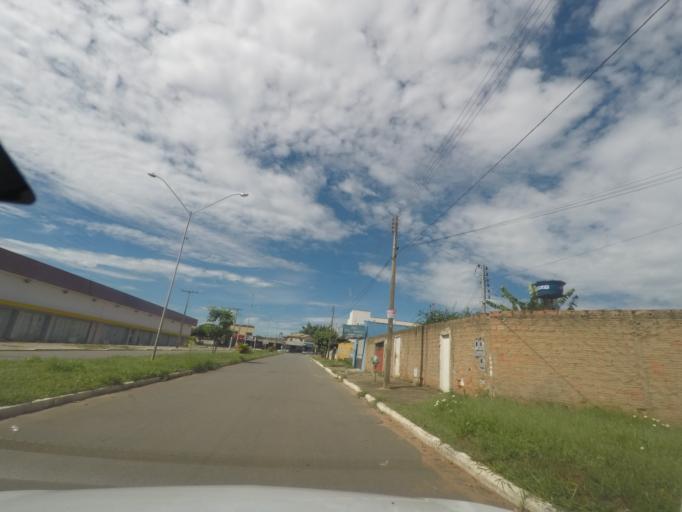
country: BR
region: Goias
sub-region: Aparecida De Goiania
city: Aparecida de Goiania
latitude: -16.8201
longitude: -49.2916
